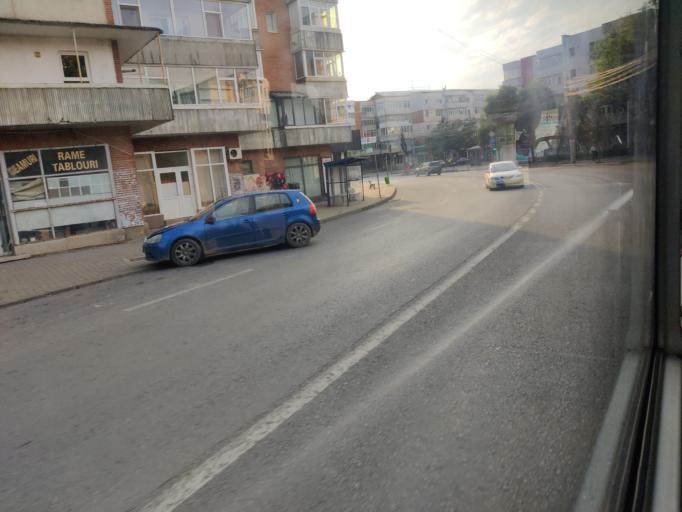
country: RO
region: Iasi
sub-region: Municipiul Iasi
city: Iasi
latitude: 47.1668
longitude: 27.5955
